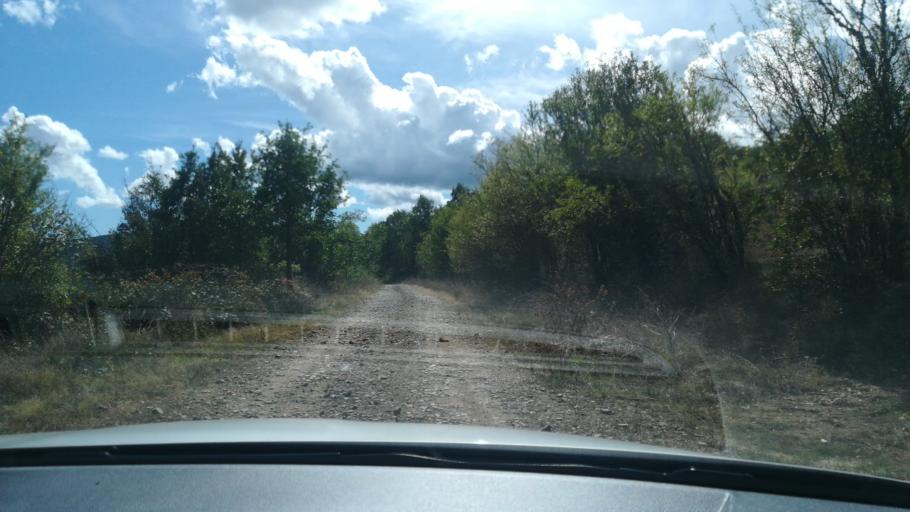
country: MK
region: Delcevo
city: Delcevo
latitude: 41.9003
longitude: 22.8055
